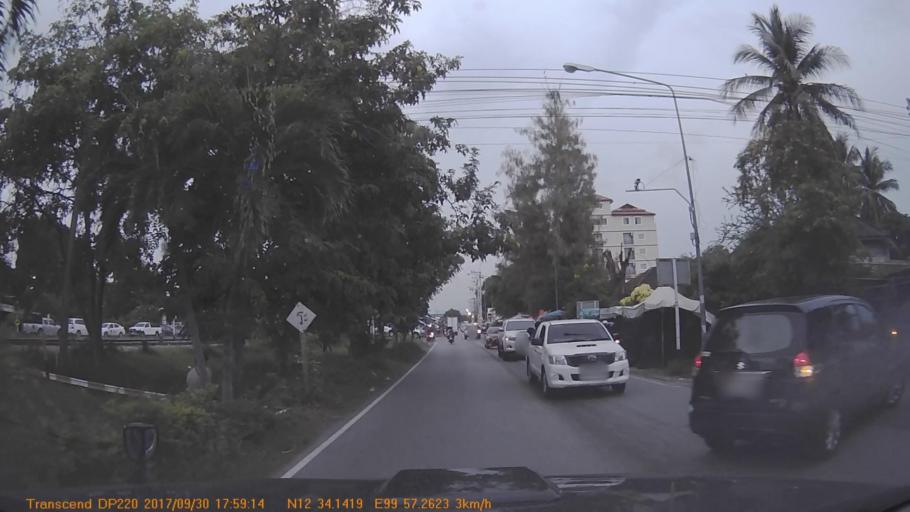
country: TH
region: Prachuap Khiri Khan
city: Hua Hin
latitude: 12.5690
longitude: 99.9544
